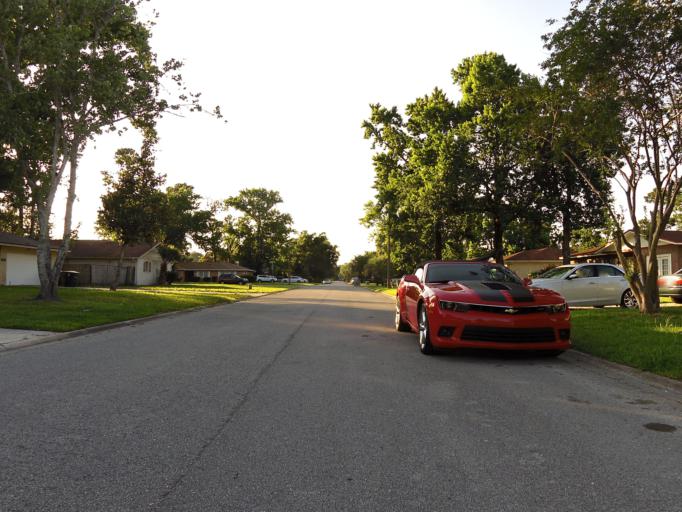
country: US
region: Florida
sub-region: Duval County
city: Jacksonville
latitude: 30.2375
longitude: -81.6017
